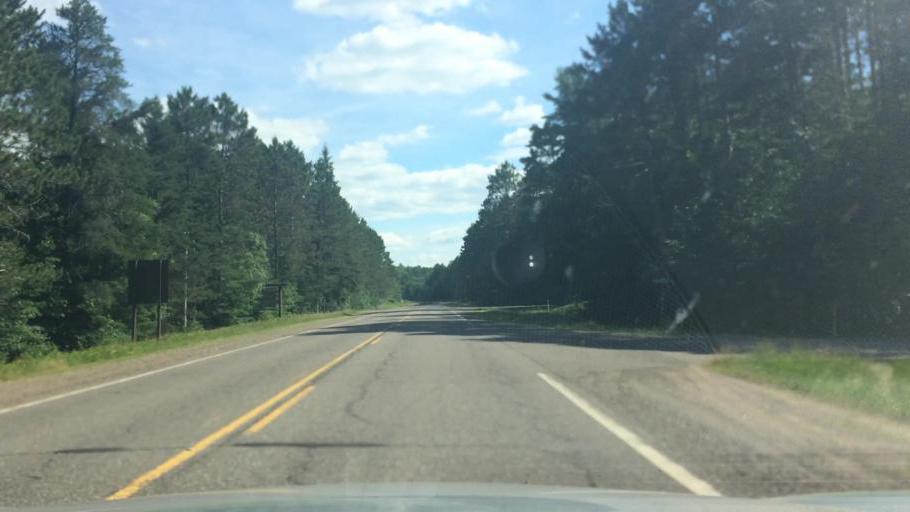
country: US
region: Wisconsin
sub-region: Vilas County
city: Lac du Flambeau
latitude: 46.0517
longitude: -89.6499
